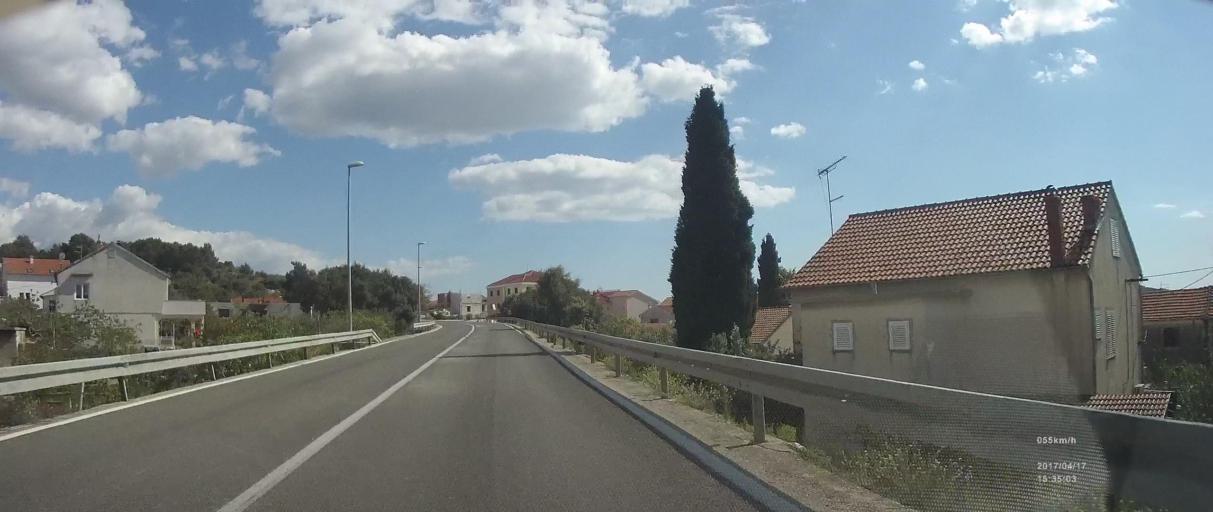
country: HR
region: Sibensko-Kniniska
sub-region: Grad Sibenik
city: Brodarica
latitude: 43.6761
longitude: 15.9225
